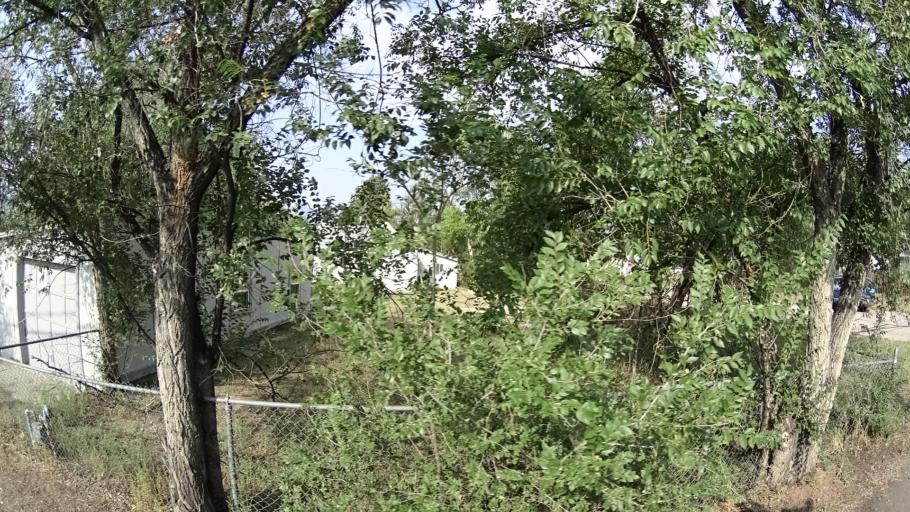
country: US
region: Colorado
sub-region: El Paso County
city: Colorado Springs
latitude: 38.8475
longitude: -104.7866
